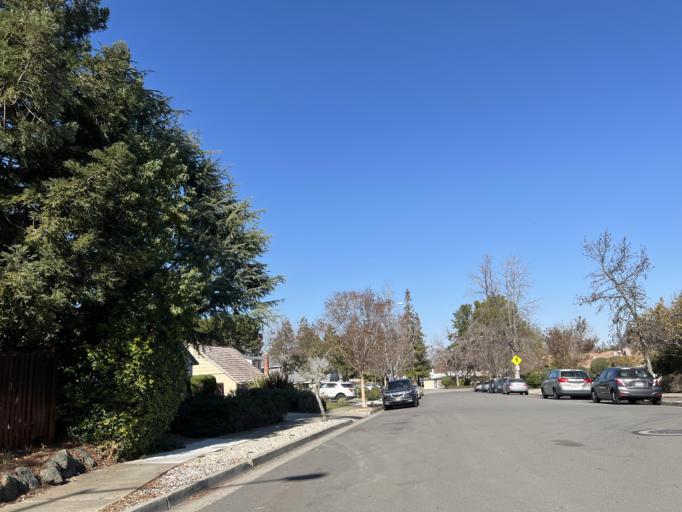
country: US
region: California
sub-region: Santa Clara County
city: Cupertino
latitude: 37.3169
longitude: -122.0702
